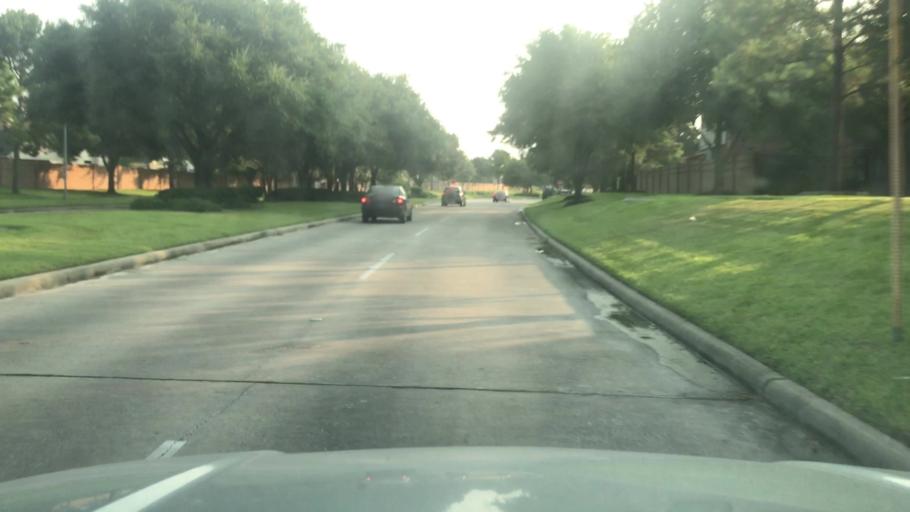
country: US
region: Texas
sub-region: Fort Bend County
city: Cinco Ranch
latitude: 29.7480
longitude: -95.7875
